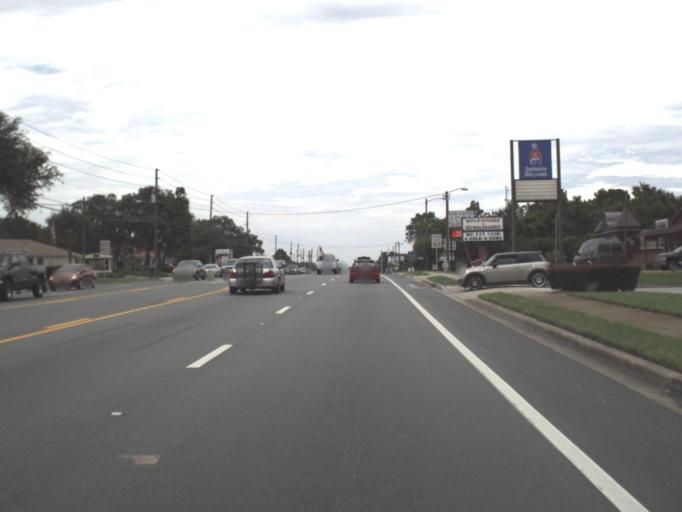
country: US
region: Florida
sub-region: Citrus County
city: Inverness Highlands North
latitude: 28.8414
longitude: -82.3617
